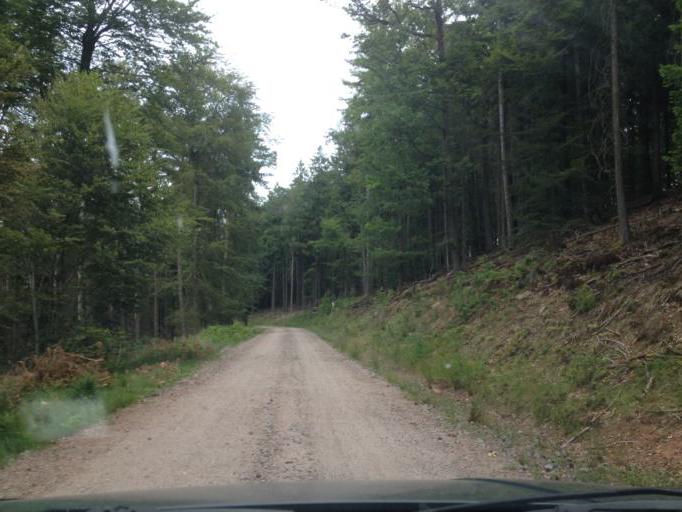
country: DE
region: Rheinland-Pfalz
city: Wilgartswiesen
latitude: 49.3019
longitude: 7.8745
